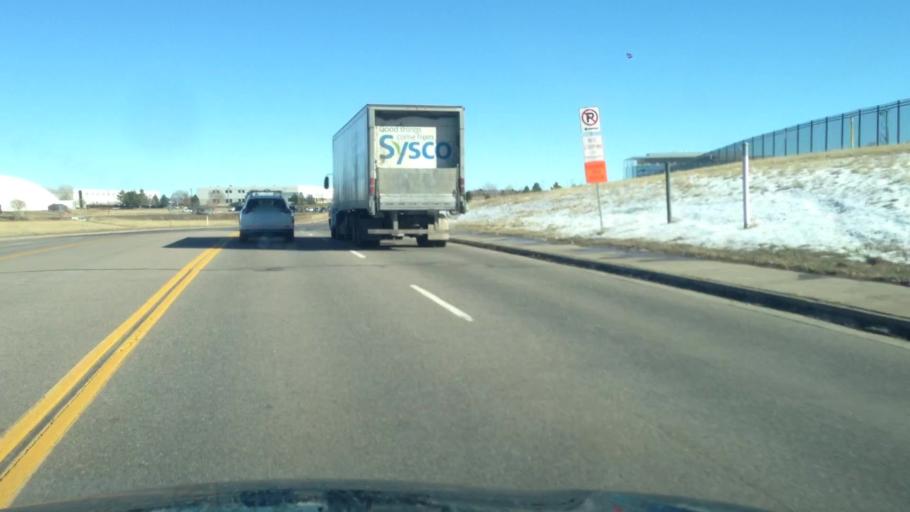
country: US
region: Colorado
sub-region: Arapahoe County
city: Centennial
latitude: 39.5880
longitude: -104.8536
